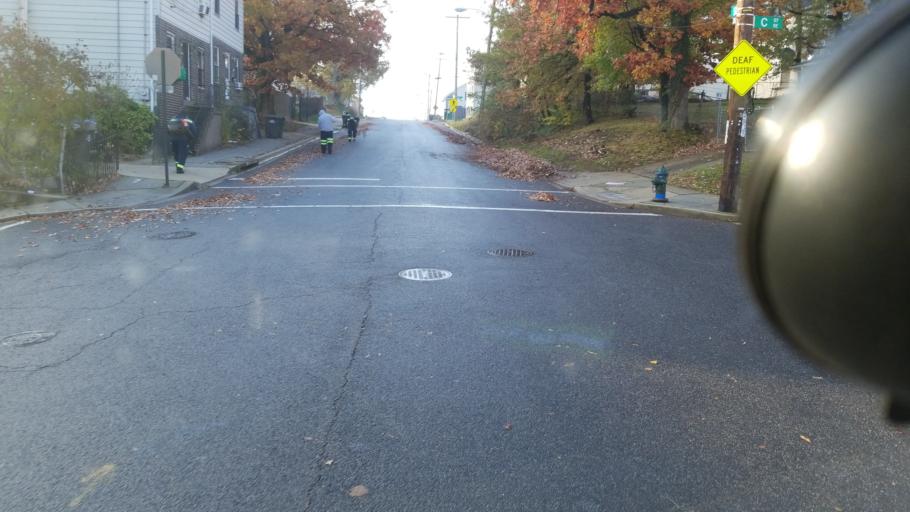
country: US
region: Maryland
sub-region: Prince George's County
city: Capitol Heights
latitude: 38.8851
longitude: -76.9284
